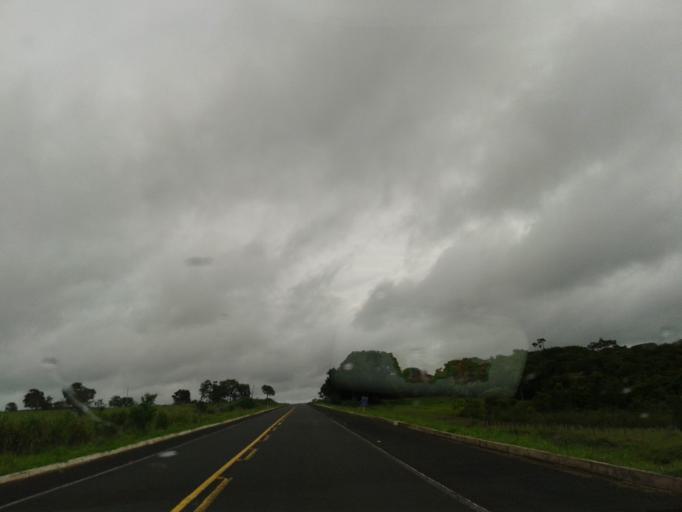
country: BR
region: Minas Gerais
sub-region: Santa Vitoria
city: Santa Vitoria
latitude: -19.2316
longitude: -50.0179
